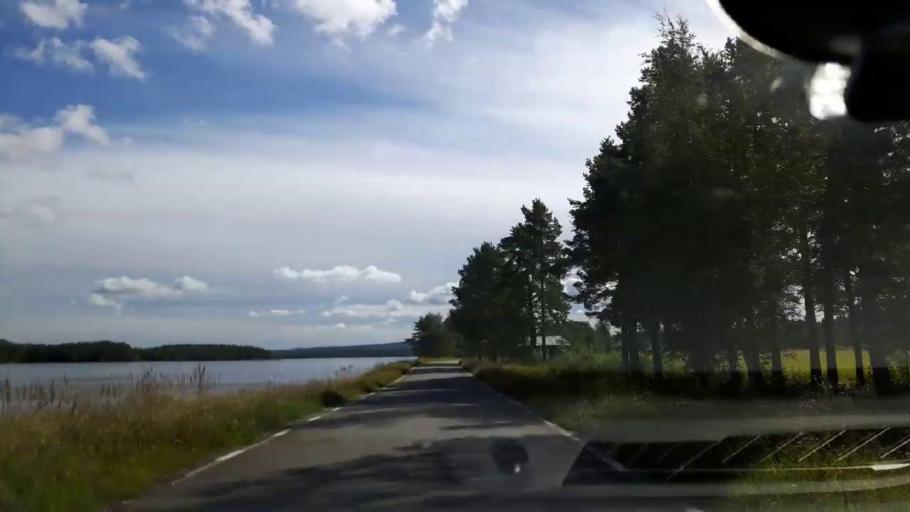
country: SE
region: Jaemtland
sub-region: Braecke Kommun
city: Braecke
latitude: 63.2123
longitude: 15.3461
